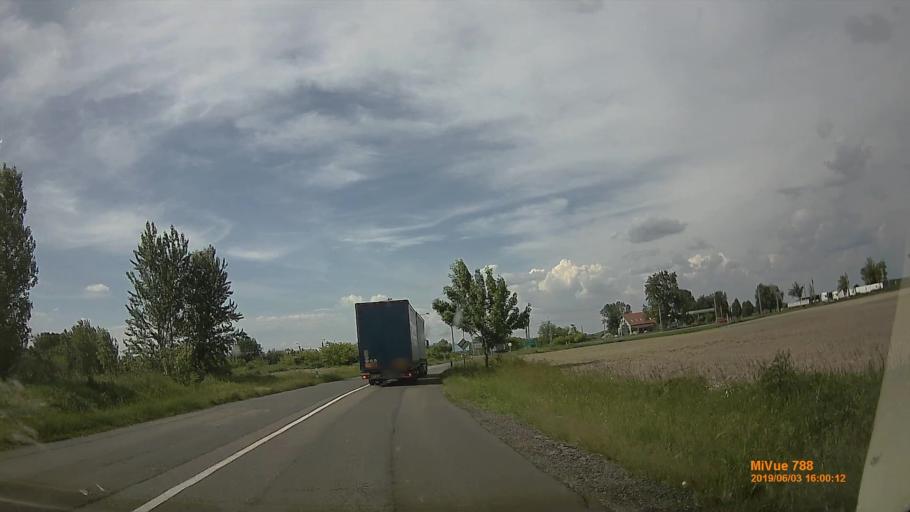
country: HU
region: Bacs-Kiskun
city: Solt
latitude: 46.7959
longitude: 19.0439
